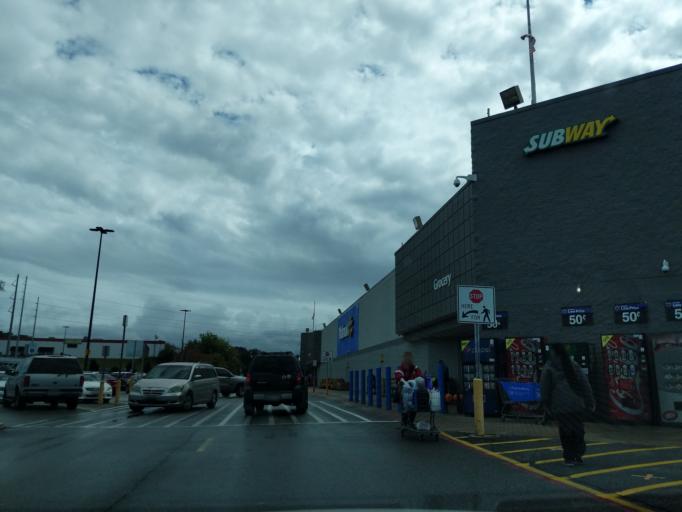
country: US
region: Alabama
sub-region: Tuscaloosa County
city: Tuscaloosa
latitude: 33.1659
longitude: -87.5193
